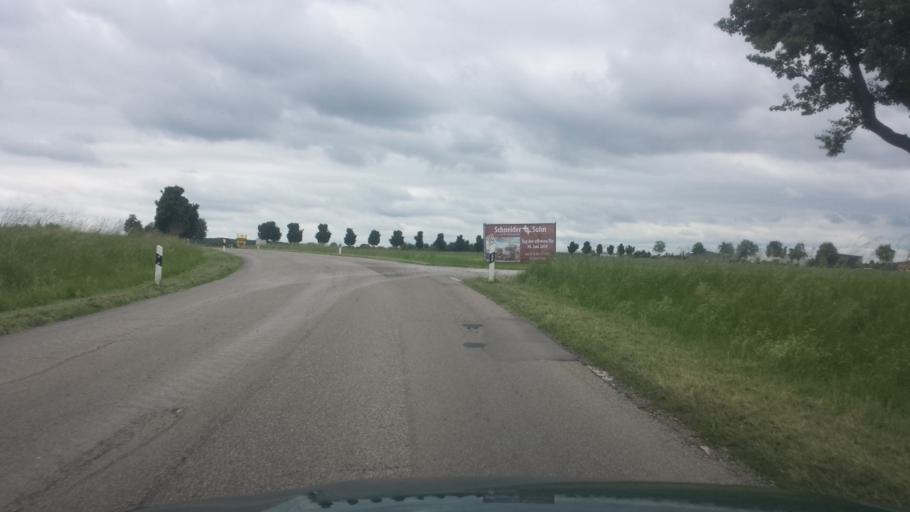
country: DE
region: Baden-Wuerttemberg
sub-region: Regierungsbezirk Stuttgart
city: Rot am See
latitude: 49.2395
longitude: 10.0218
